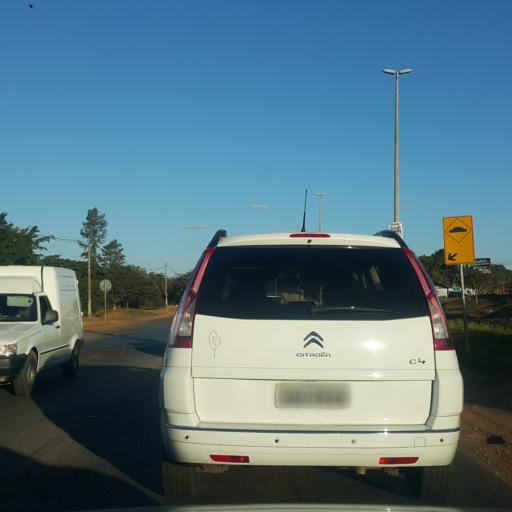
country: BR
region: Federal District
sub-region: Brasilia
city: Brasilia
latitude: -15.8633
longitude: -47.9785
